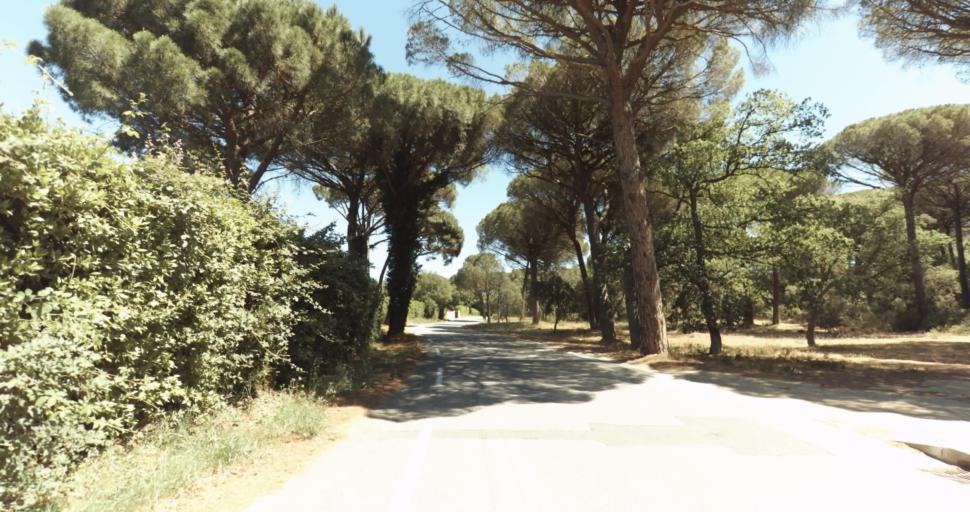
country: FR
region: Provence-Alpes-Cote d'Azur
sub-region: Departement du Var
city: Gassin
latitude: 43.2529
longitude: 6.5840
